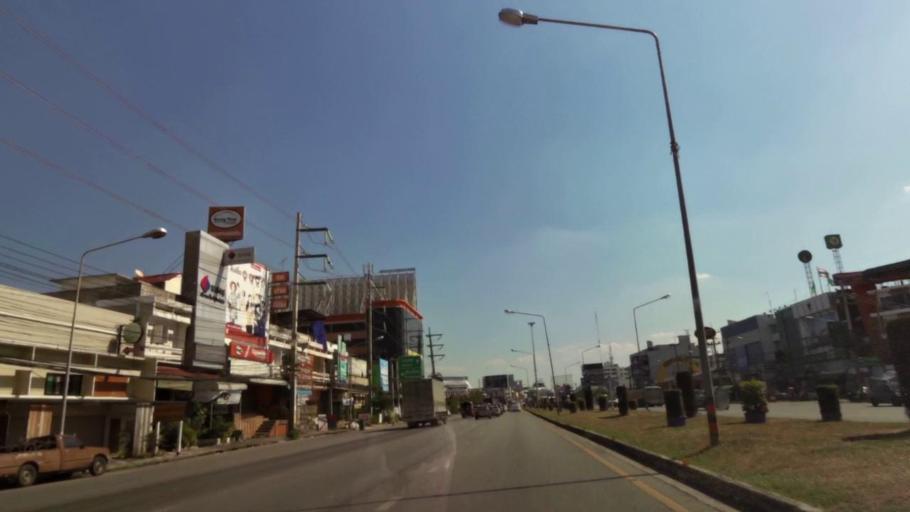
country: TH
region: Nakhon Sawan
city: Nakhon Sawan
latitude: 15.6997
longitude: 100.1190
